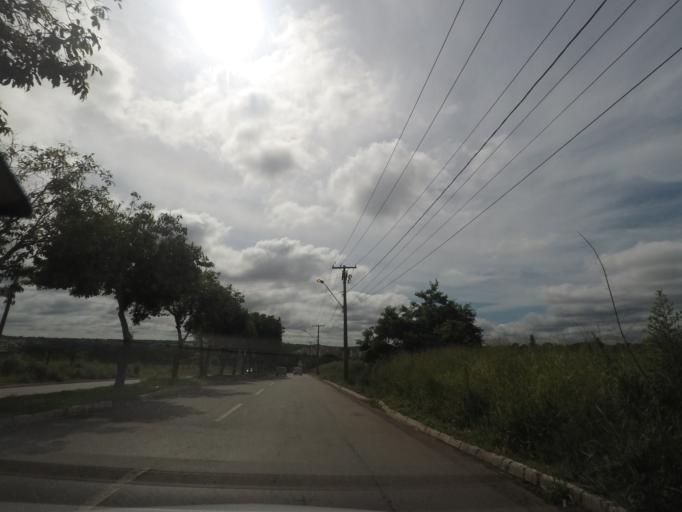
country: BR
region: Goias
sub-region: Goiania
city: Goiania
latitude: -16.6585
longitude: -49.2187
